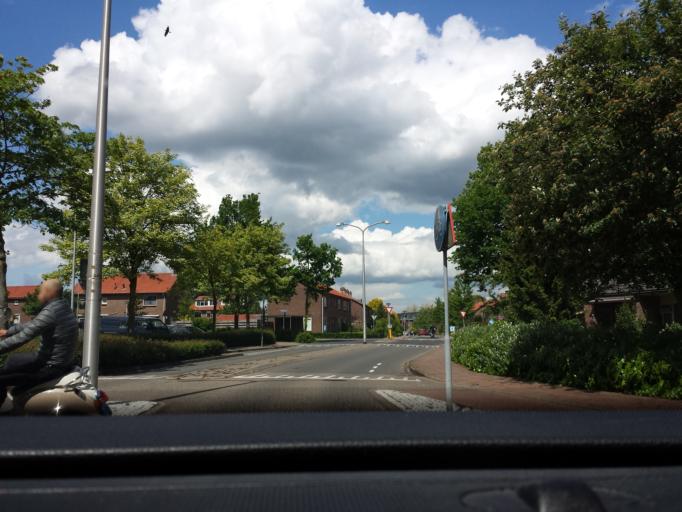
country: NL
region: Gelderland
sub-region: Gemeente Zutphen
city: Warnsveld
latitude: 52.1364
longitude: 6.2283
